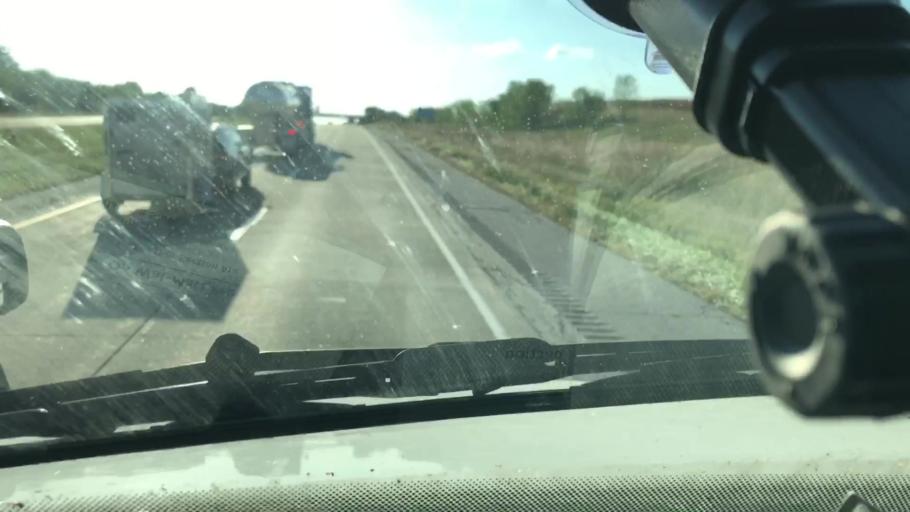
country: US
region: Iowa
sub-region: Pottawattamie County
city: Avoca
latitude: 41.4993
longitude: -95.4751
